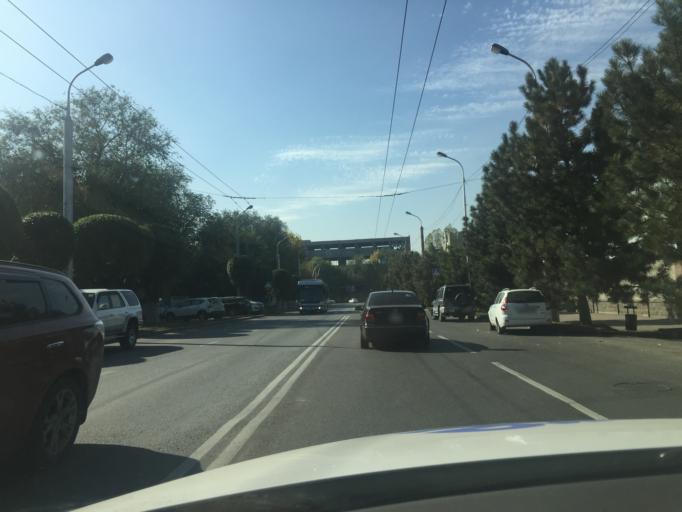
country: KZ
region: Almaty Qalasy
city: Almaty
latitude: 43.2570
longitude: 76.9042
